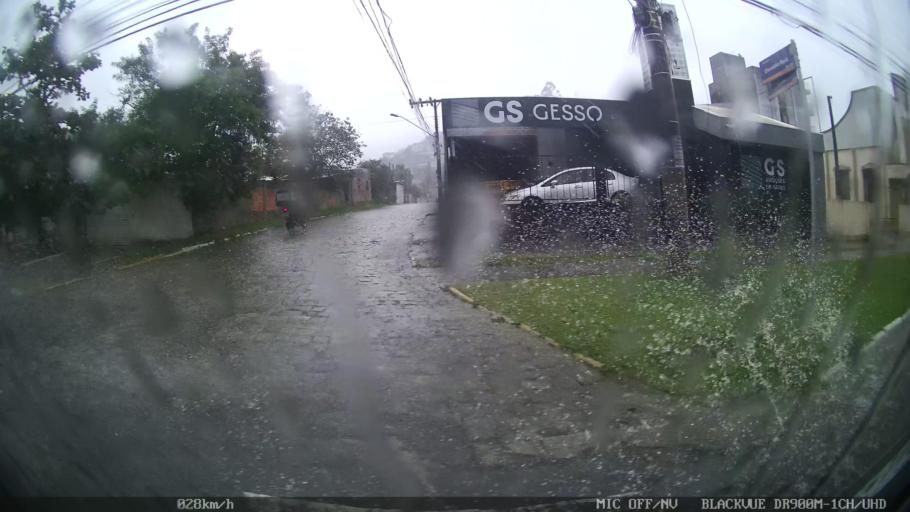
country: BR
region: Santa Catarina
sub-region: Balneario Camboriu
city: Balneario Camboriu
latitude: -26.9497
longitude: -48.6407
